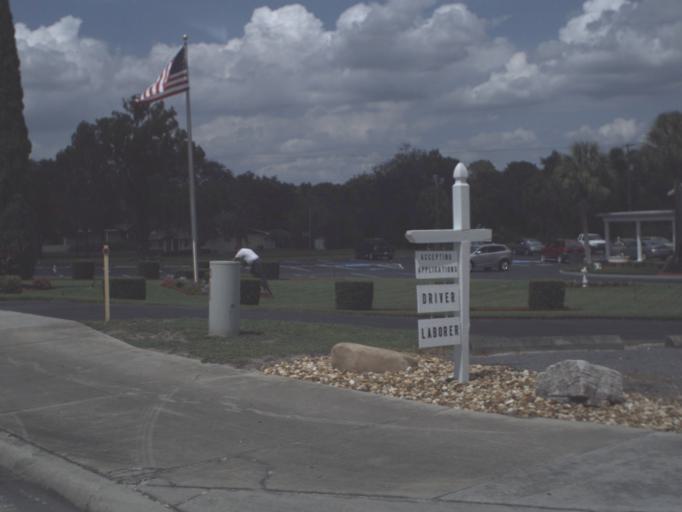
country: US
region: Florida
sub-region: Citrus County
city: Inverness
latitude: 28.8172
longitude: -82.3155
